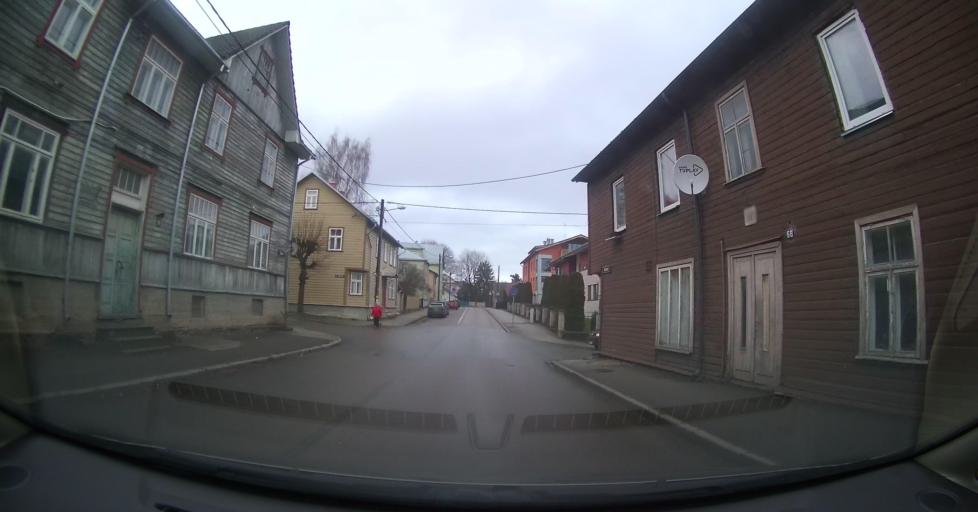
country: EE
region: Tartu
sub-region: Tartu linn
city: Tartu
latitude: 58.3690
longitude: 26.7344
